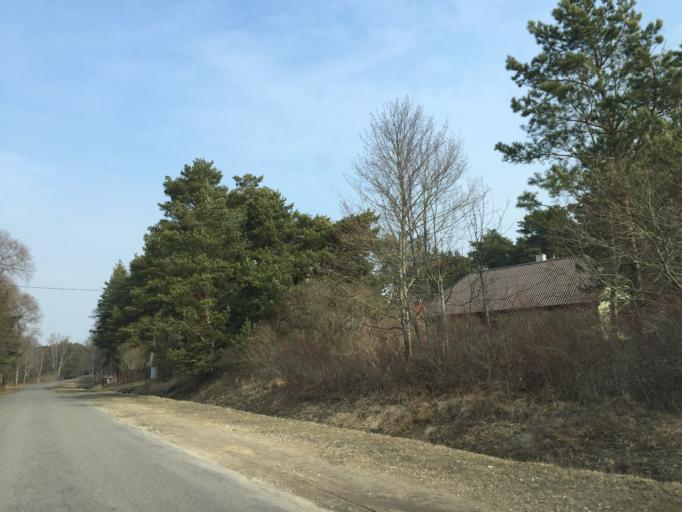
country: LV
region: Salacgrivas
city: Ainazi
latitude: 57.8791
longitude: 24.3634
